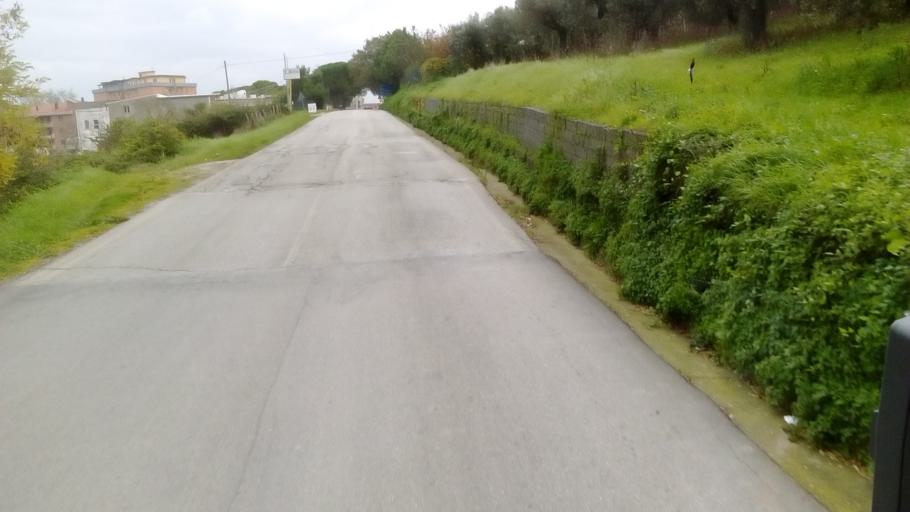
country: IT
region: Abruzzo
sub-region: Provincia di Chieti
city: San Salvo
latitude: 42.0563
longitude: 14.7303
